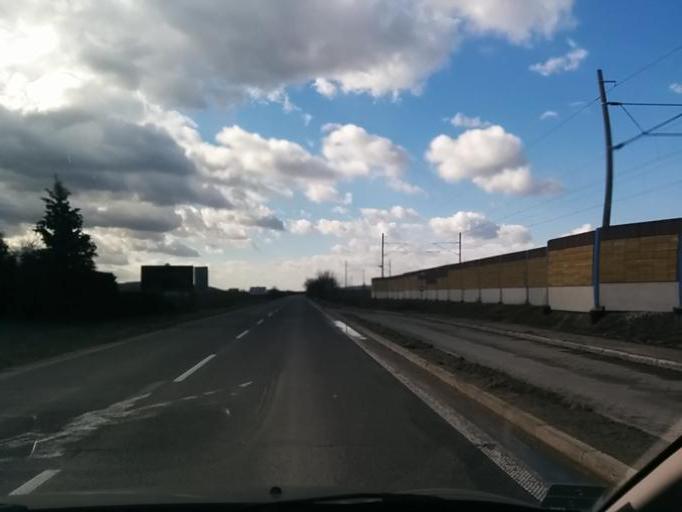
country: SK
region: Trenciansky
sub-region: Okres Trencin
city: Trencin
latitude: 48.8709
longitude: 17.9682
